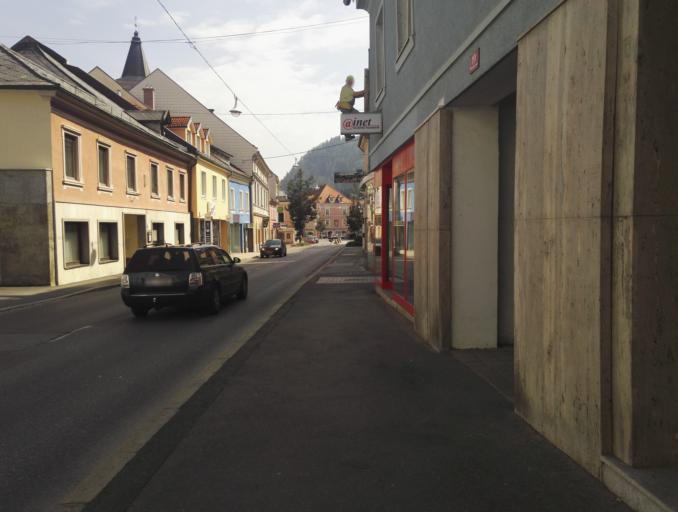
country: AT
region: Styria
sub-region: Politischer Bezirk Murtal
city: Judenburg
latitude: 47.1681
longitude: 14.6586
